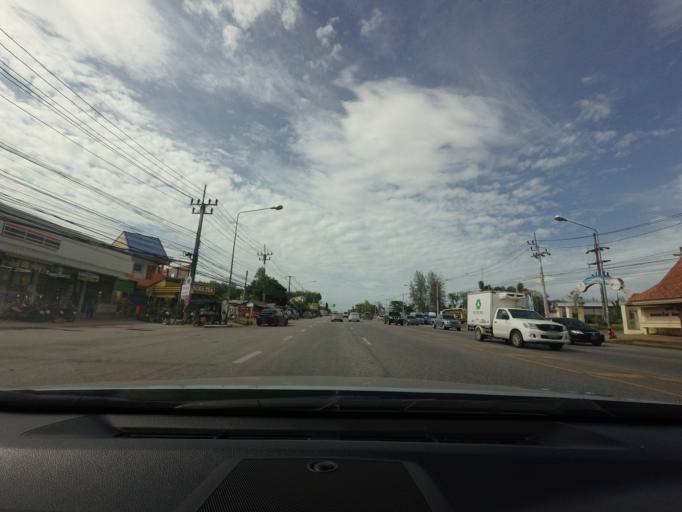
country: TH
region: Songkhla
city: Khlong Hoi Khong
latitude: 6.9571
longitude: 100.4217
